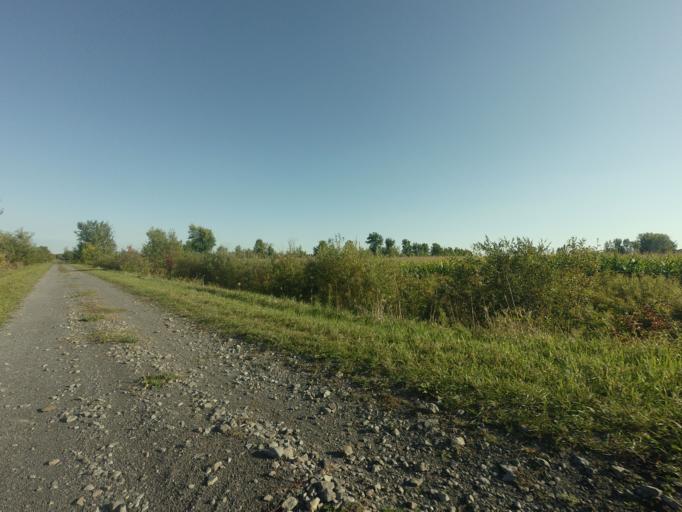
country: CA
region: Ontario
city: Hawkesbury
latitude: 45.5131
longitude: -74.5075
